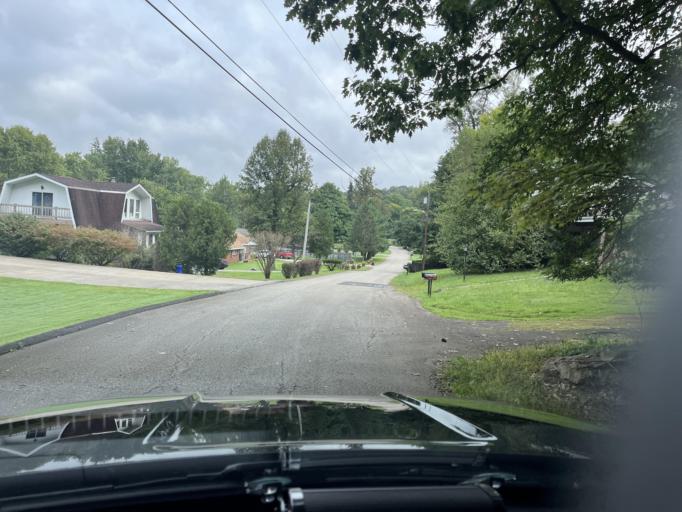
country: US
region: Pennsylvania
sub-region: Fayette County
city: Hopwood
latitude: 39.8602
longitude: -79.7006
